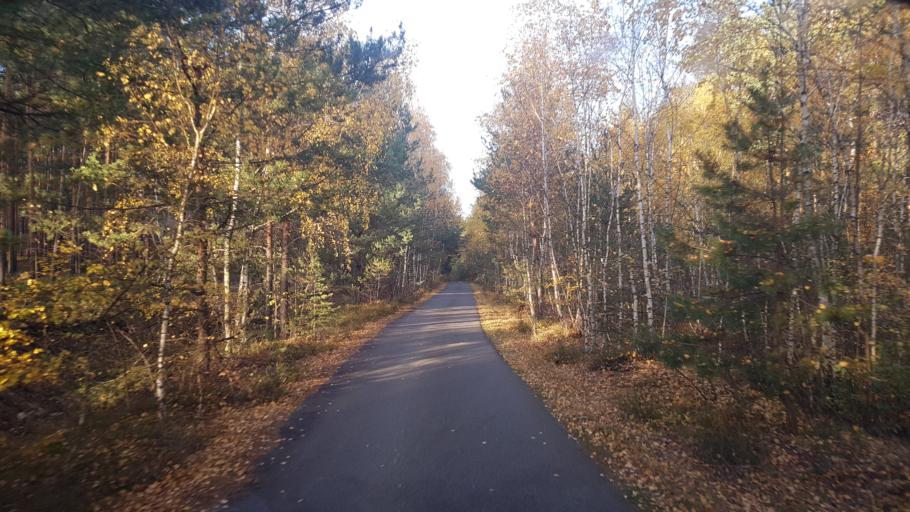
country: DE
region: Brandenburg
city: Calau
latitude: 51.7101
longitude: 13.9492
